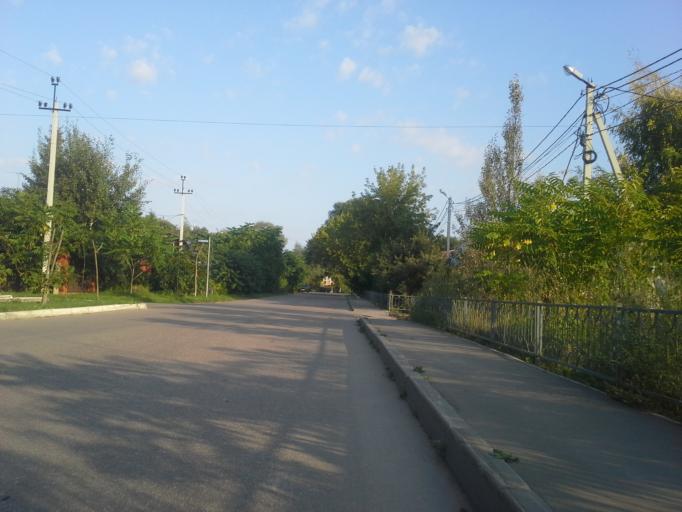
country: RU
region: Moskovskaya
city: Filimonki
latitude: 55.5192
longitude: 37.3676
